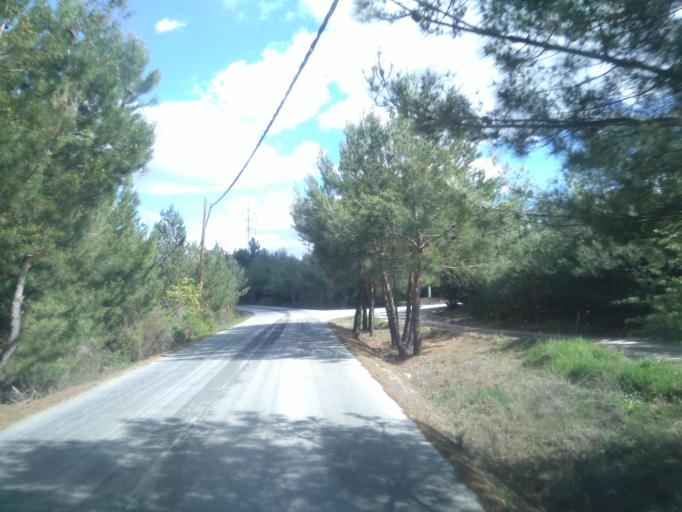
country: GR
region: Central Macedonia
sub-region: Nomos Thessalonikis
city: Asvestochori
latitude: 40.6412
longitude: 23.0065
